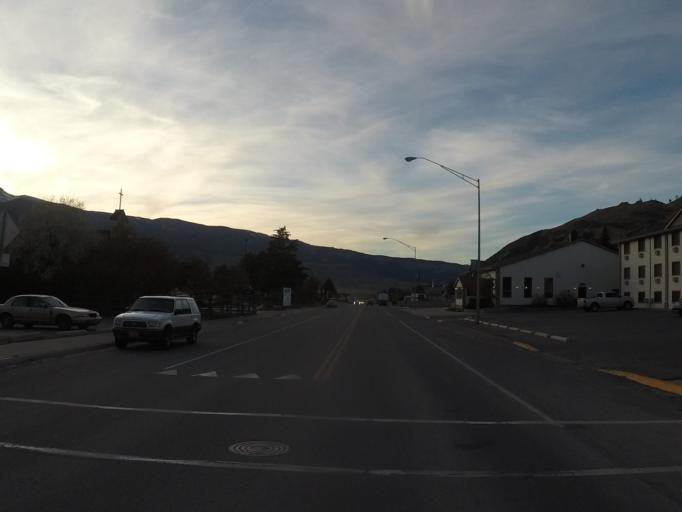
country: US
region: Montana
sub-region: Gallatin County
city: West Yellowstone
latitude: 45.0348
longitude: -110.7104
